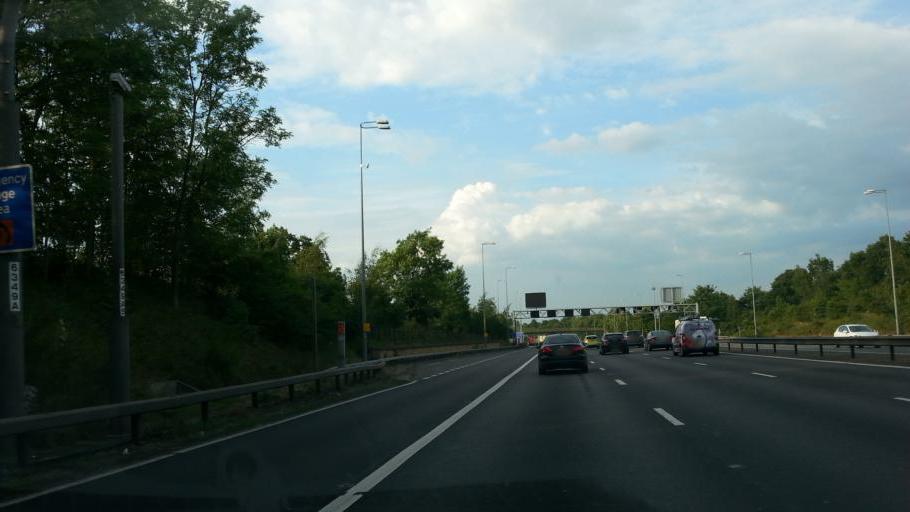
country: GB
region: England
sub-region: Solihull
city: Solihull
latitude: 52.3931
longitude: -1.7699
